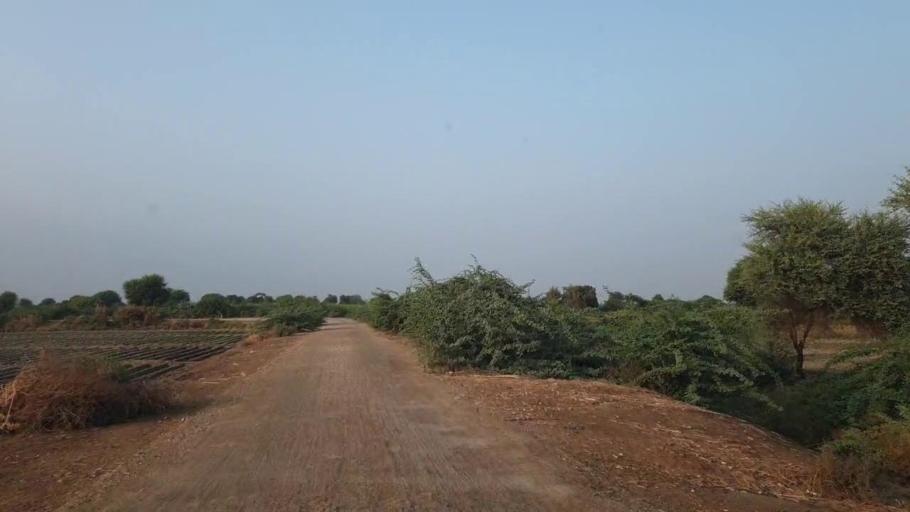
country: PK
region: Sindh
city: Tando Ghulam Ali
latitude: 25.0660
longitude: 68.9605
